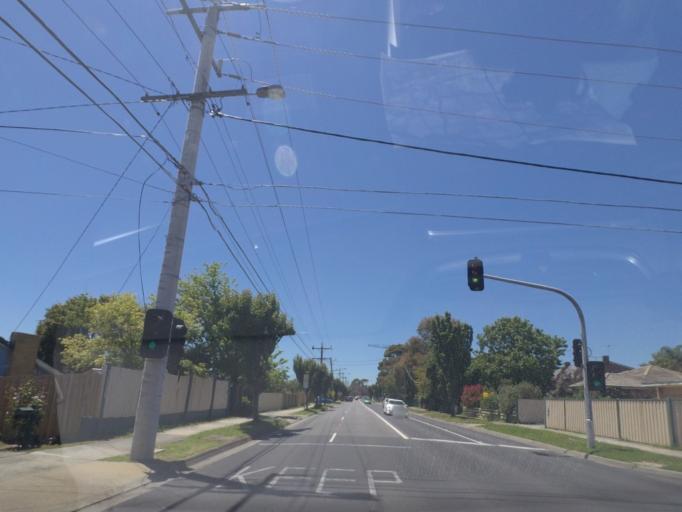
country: AU
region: Victoria
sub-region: Banyule
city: Bundoora
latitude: -37.6973
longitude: 145.0550
